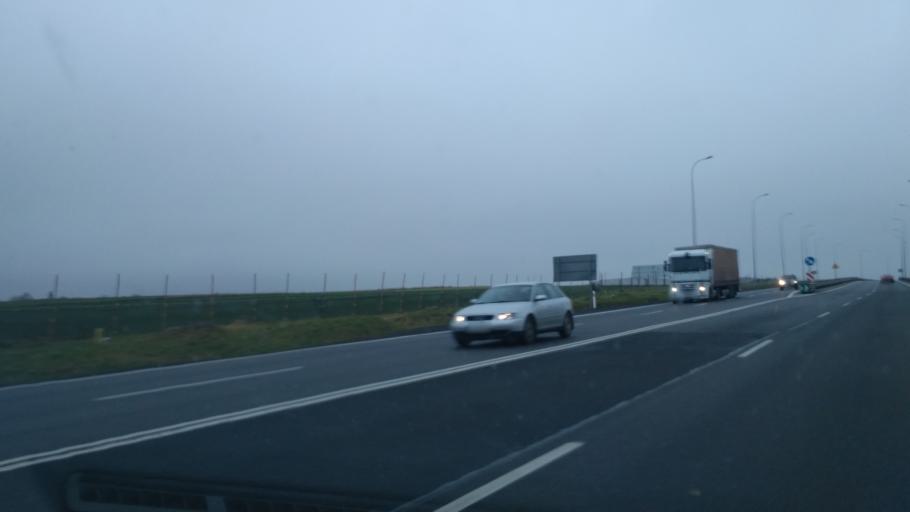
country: PL
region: Subcarpathian Voivodeship
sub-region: Powiat jaroslawski
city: Wierzbna
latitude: 50.0349
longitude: 22.5880
